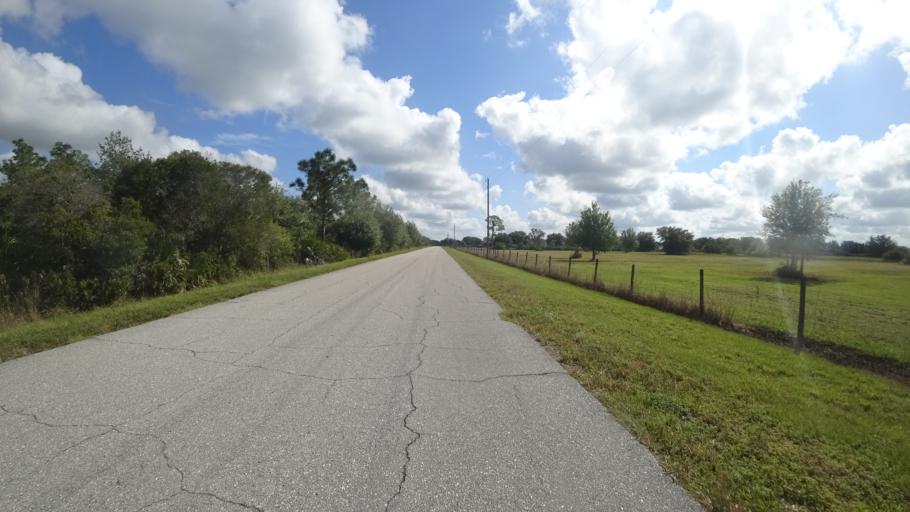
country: US
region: Florida
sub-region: Sarasota County
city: Fruitville
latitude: 27.4050
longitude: -82.2747
